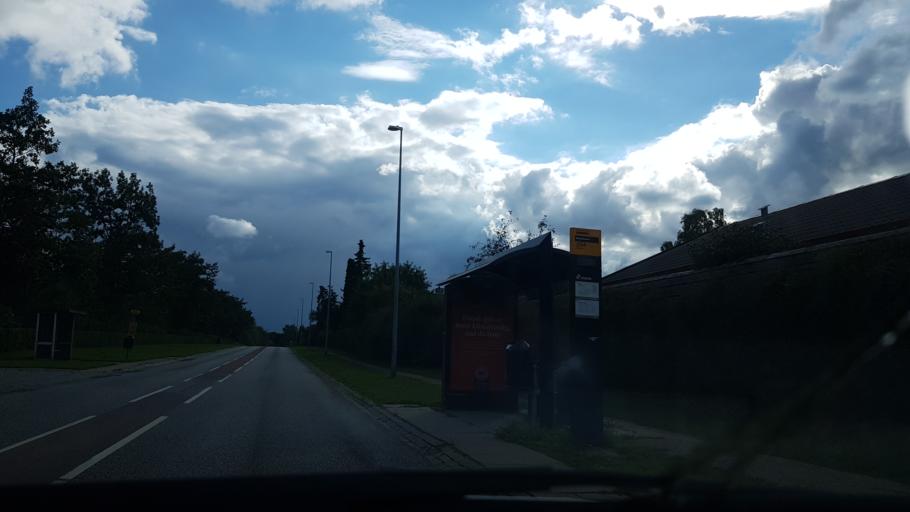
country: DK
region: Capital Region
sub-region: Fredensborg Kommune
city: Kokkedal
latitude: 55.9162
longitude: 12.4944
